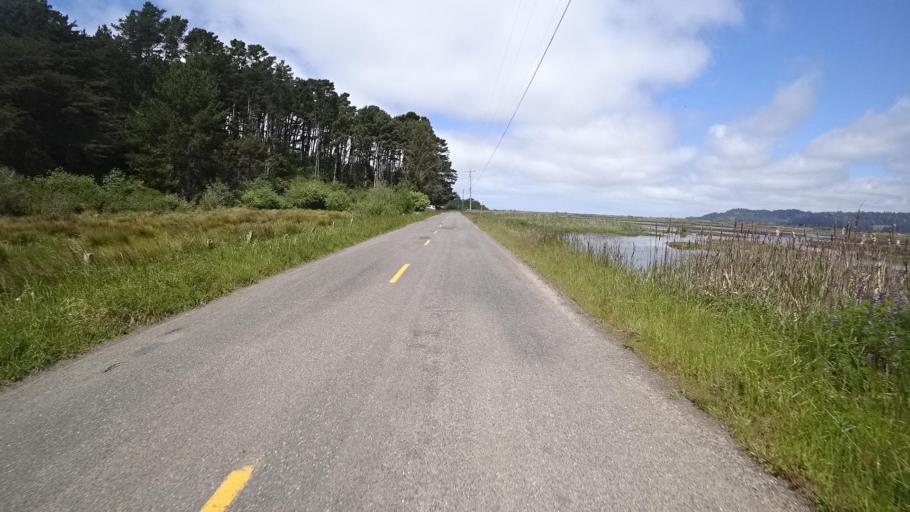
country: US
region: California
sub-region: Humboldt County
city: Humboldt Hill
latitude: 40.6804
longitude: -124.2295
